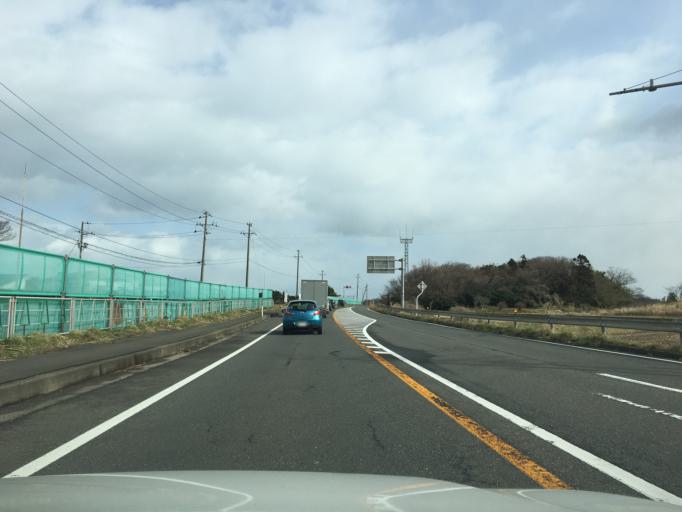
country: JP
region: Yamagata
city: Yuza
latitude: 39.2726
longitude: 139.9240
